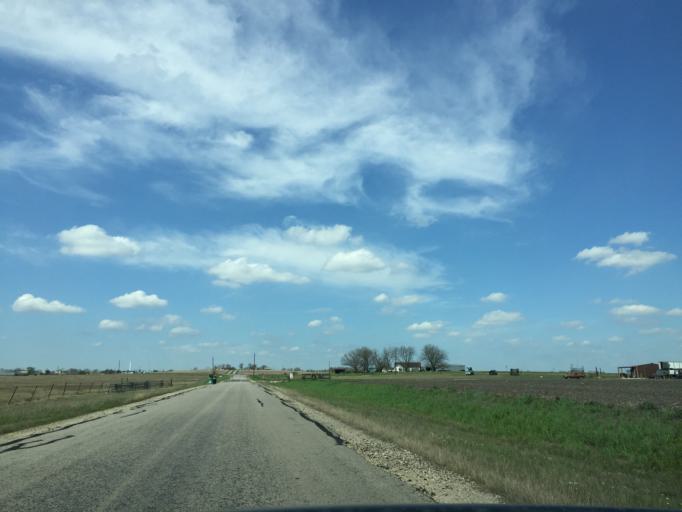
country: US
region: Texas
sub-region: Milam County
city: Thorndale
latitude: 30.5519
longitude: -97.2978
